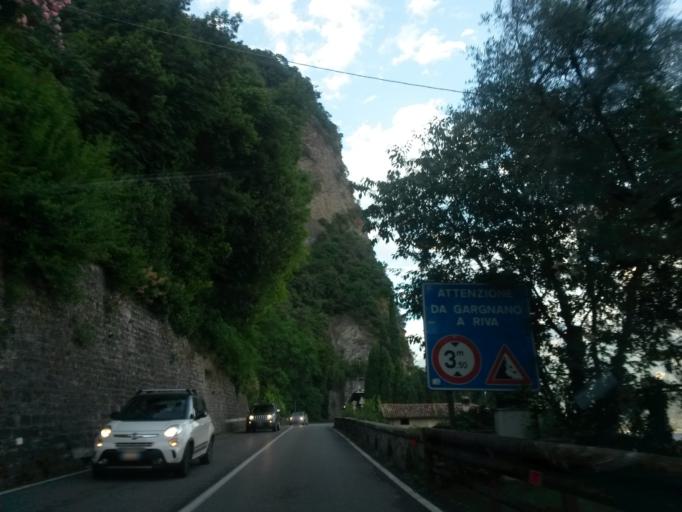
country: IT
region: Lombardy
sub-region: Provincia di Brescia
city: Gargnano
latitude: 45.7029
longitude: 10.6808
